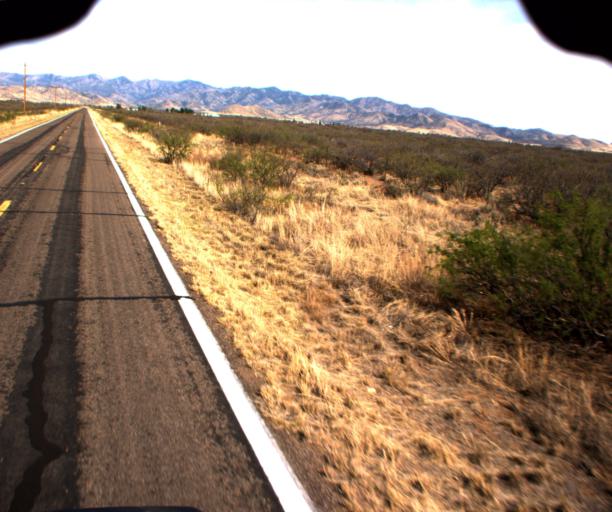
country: US
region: Arizona
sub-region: Cochise County
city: Willcox
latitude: 31.8760
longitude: -109.5140
